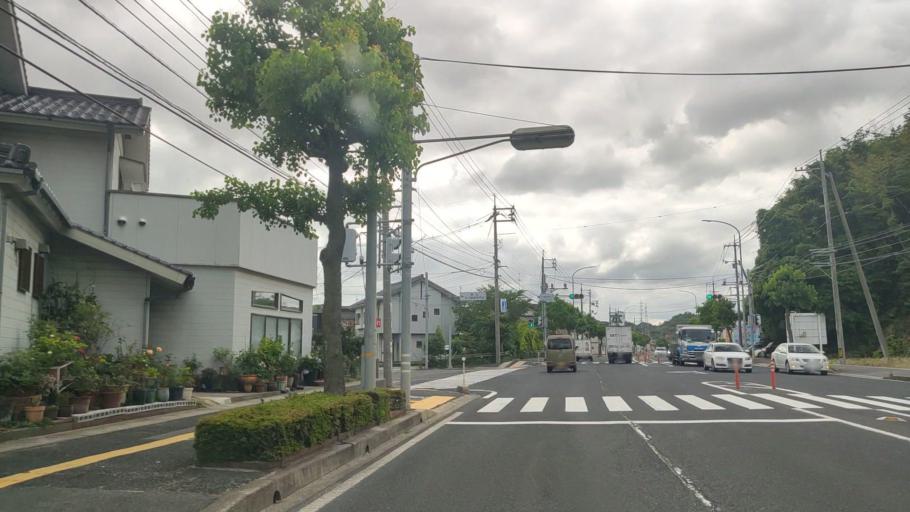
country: JP
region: Tottori
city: Yonago
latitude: 35.4237
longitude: 133.3463
